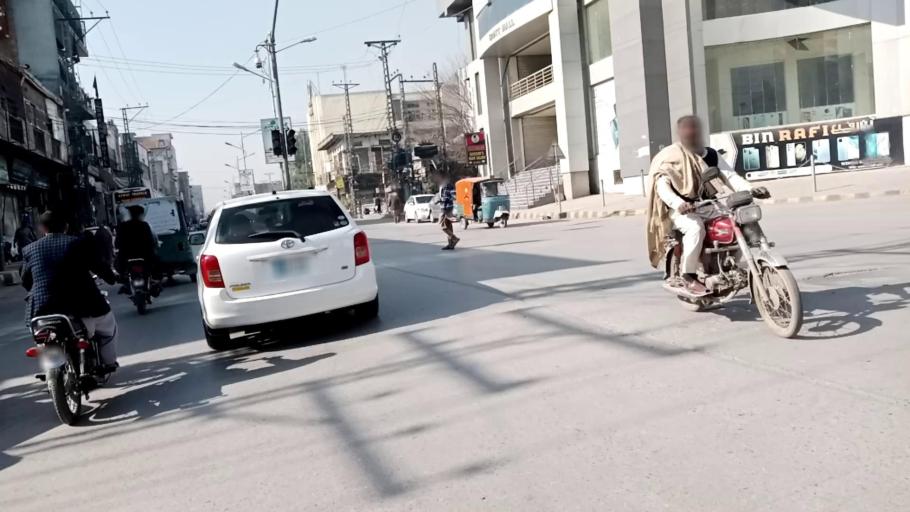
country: PK
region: Khyber Pakhtunkhwa
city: Peshawar
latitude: 34.0004
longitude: 71.5427
